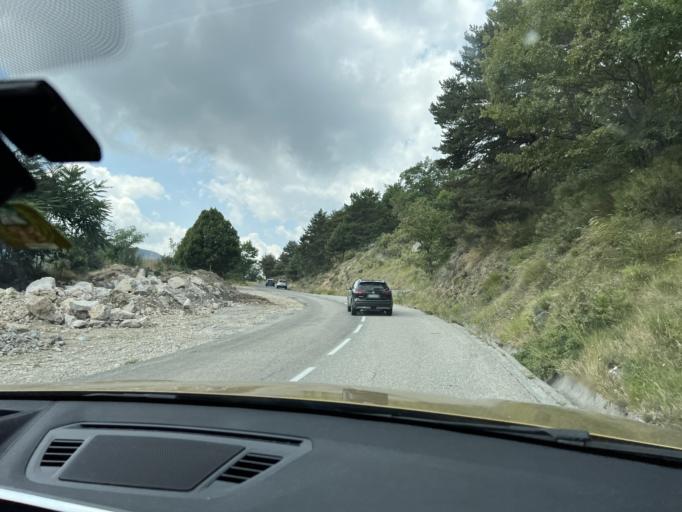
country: FR
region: Provence-Alpes-Cote d'Azur
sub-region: Departement des Alpes-Maritimes
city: Grasse
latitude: 43.7975
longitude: 6.9310
